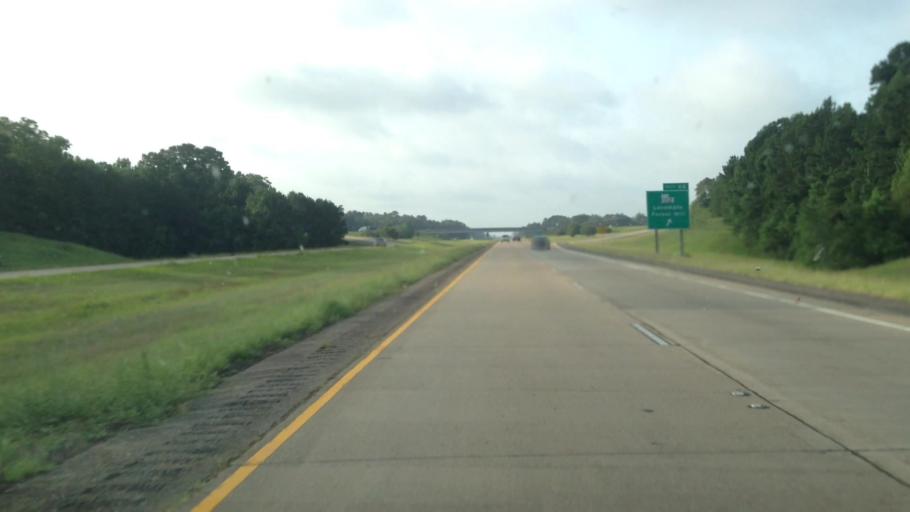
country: US
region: Louisiana
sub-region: Rapides Parish
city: Lecompte
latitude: 31.0771
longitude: -92.4368
